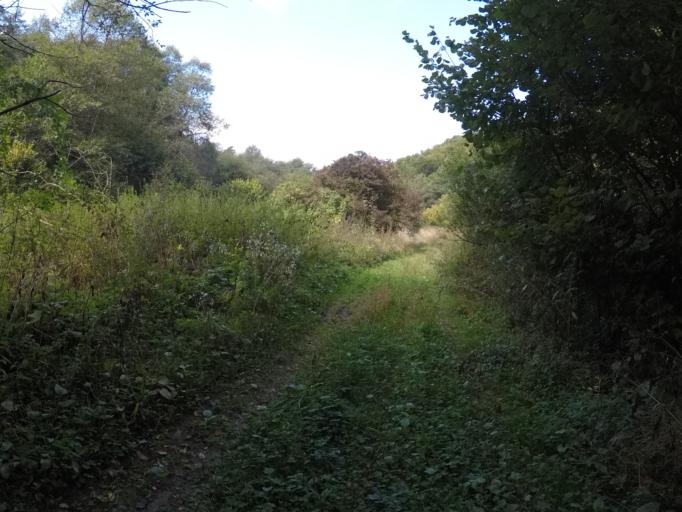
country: SK
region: Presovsky
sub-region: Okres Presov
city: Presov
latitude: 48.9323
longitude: 21.1653
